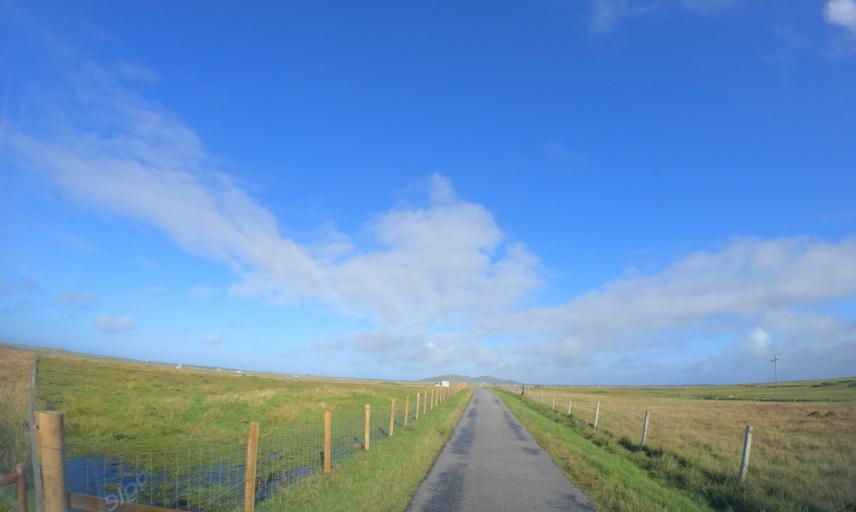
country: GB
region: Scotland
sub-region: Eilean Siar
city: Barra
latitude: 56.4756
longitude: -6.9260
